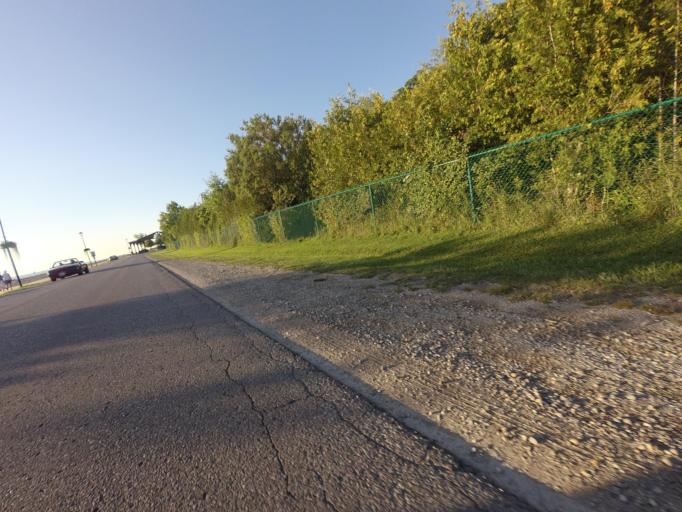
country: CA
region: Ontario
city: Goderich
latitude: 43.7365
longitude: -81.7255
